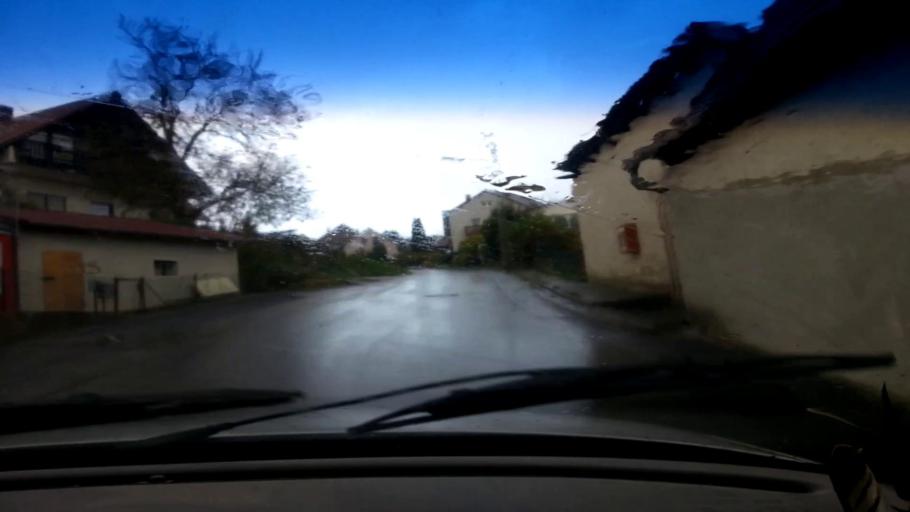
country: DE
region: Bavaria
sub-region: Upper Franconia
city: Priesendorf
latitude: 49.8634
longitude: 10.7225
